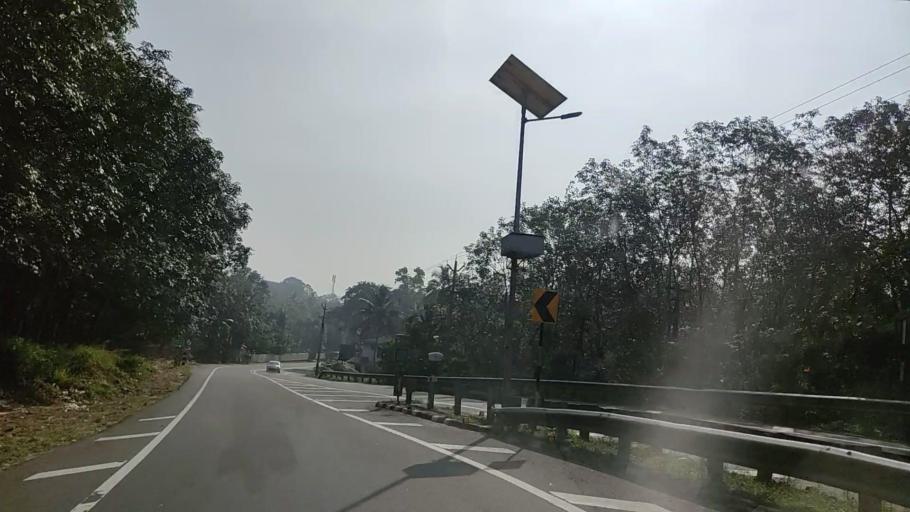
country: IN
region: Kerala
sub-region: Kollam
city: Punalur
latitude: 8.9763
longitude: 76.8152
